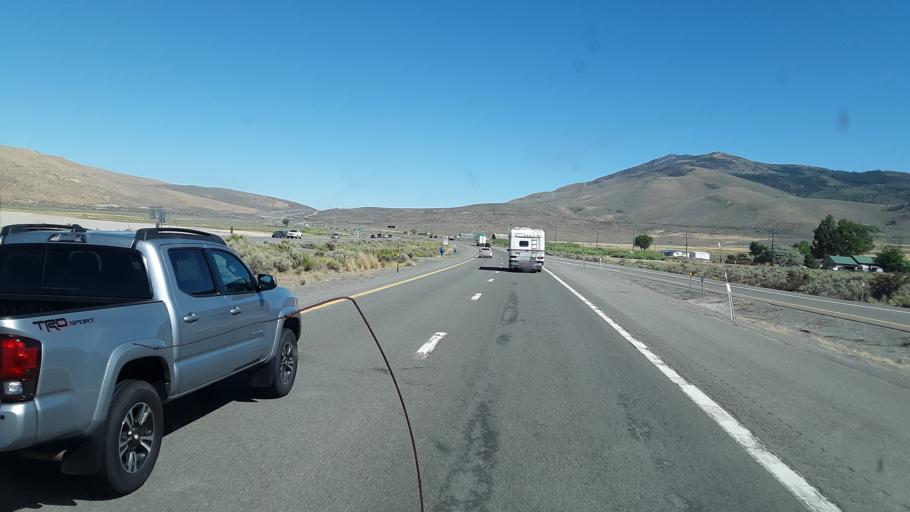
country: US
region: Nevada
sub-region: Washoe County
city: Cold Springs
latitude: 39.6537
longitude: -119.9840
